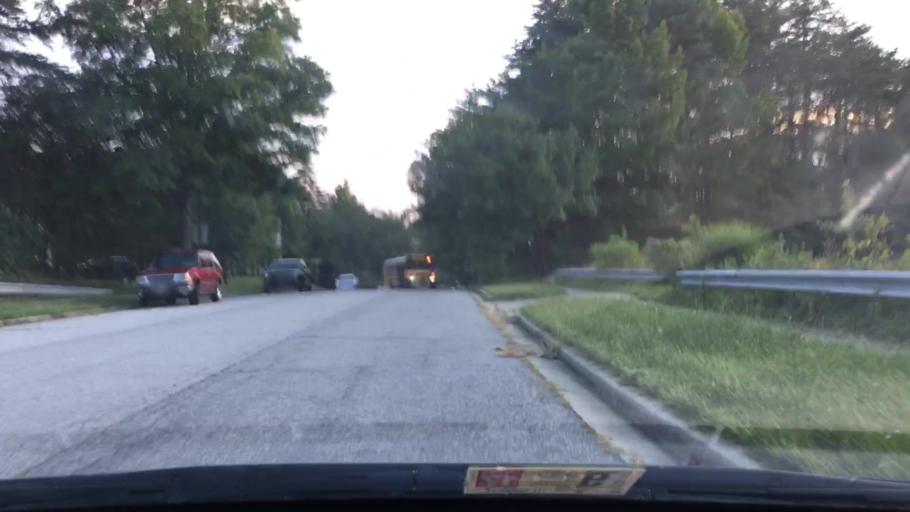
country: US
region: Maryland
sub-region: Prince George's County
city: South Laurel
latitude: 39.0493
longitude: -76.8291
